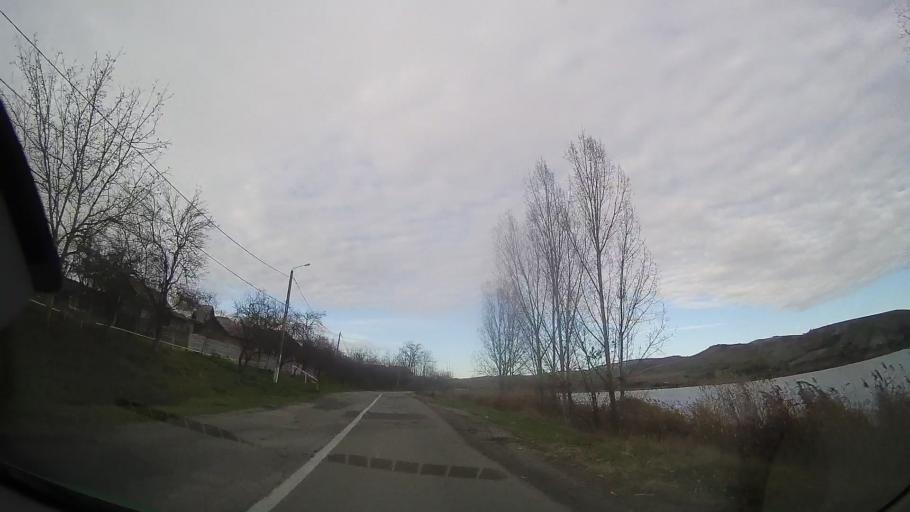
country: RO
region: Cluj
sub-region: Comuna Geaca
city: Geaca
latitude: 46.8400
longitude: 24.1271
